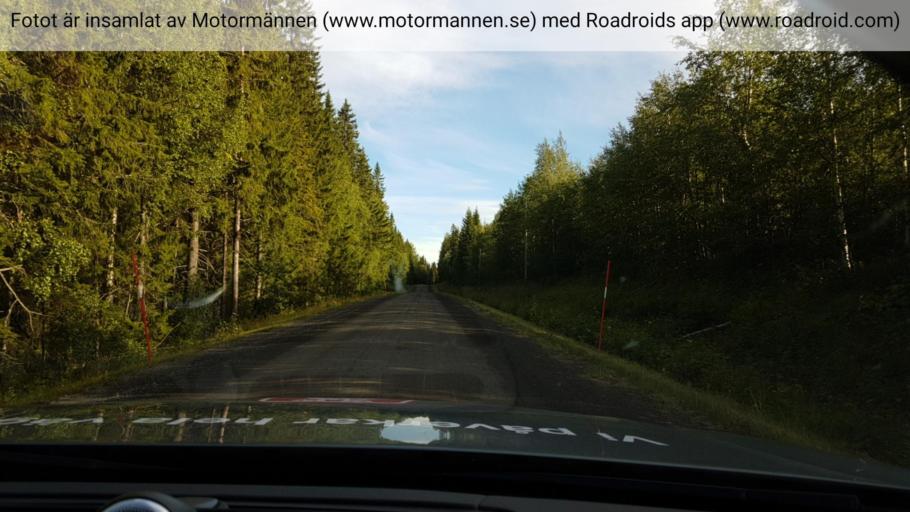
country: SE
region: Jaemtland
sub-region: Stroemsunds Kommun
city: Stroemsund
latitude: 64.1045
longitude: 15.8209
